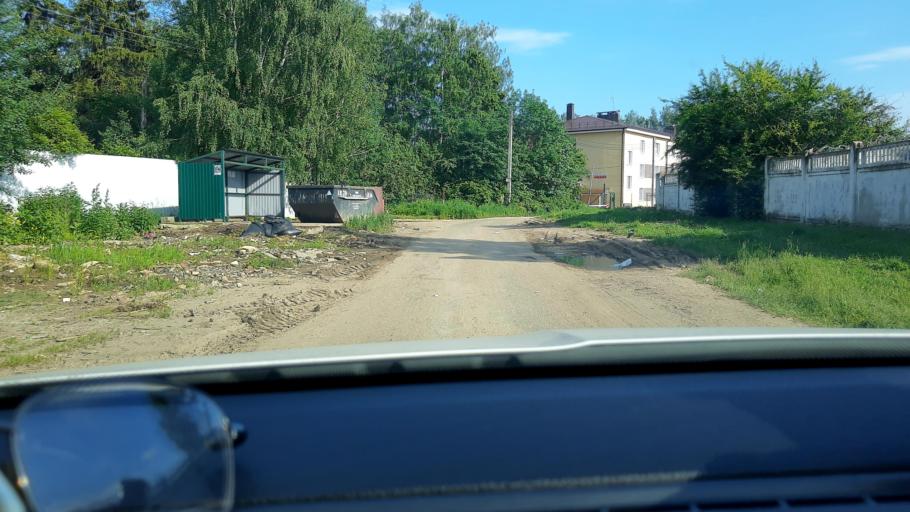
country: RU
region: Moscow
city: Novo-Peredelkino
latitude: 55.6688
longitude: 37.3222
